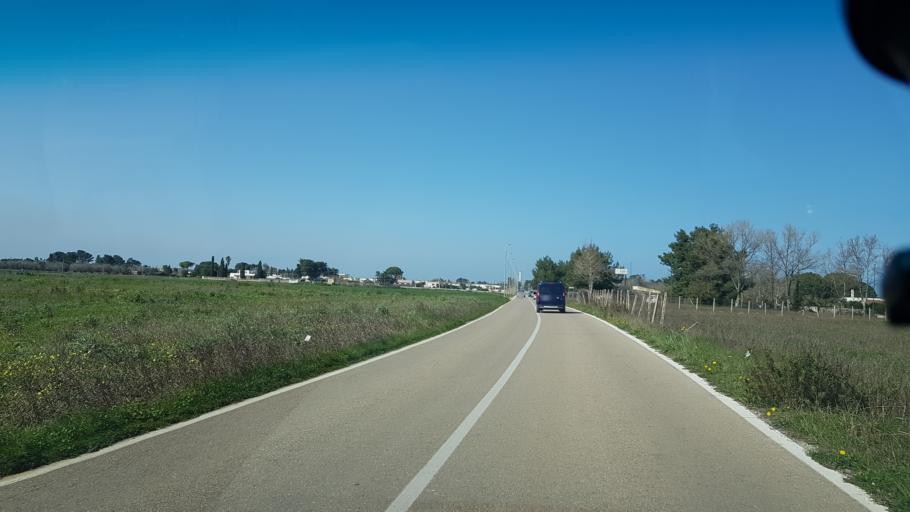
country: IT
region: Apulia
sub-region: Provincia di Brindisi
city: Torchiarolo
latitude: 40.5124
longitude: 18.0870
